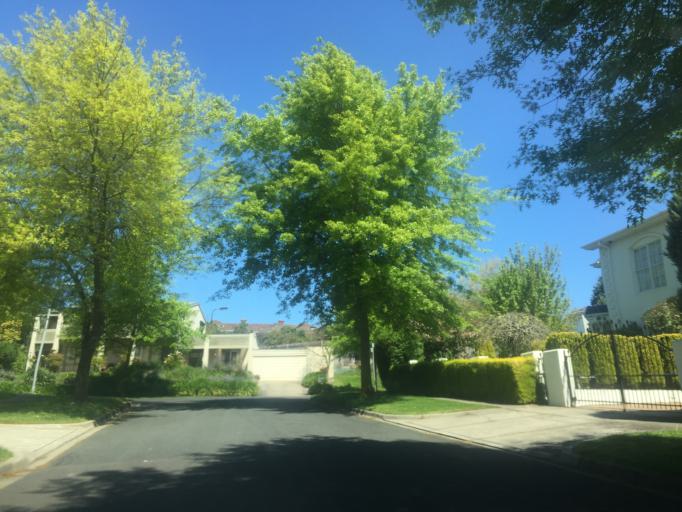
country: AU
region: Victoria
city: Mont Albert
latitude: -37.8083
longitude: 145.0877
